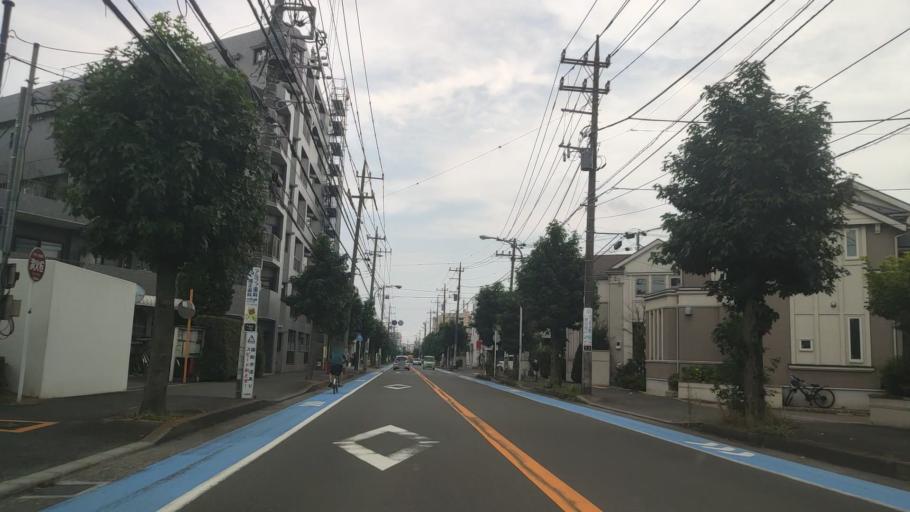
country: JP
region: Kanagawa
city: Minami-rinkan
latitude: 35.5004
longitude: 139.4504
